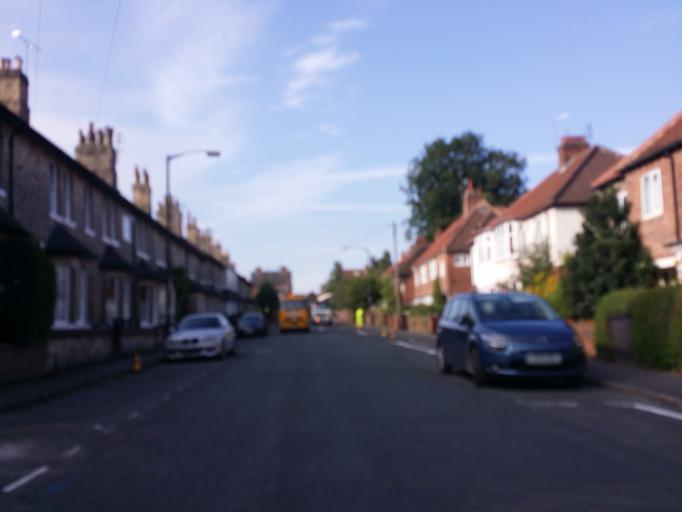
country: GB
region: England
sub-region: City of York
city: York
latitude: 53.9673
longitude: -1.0887
